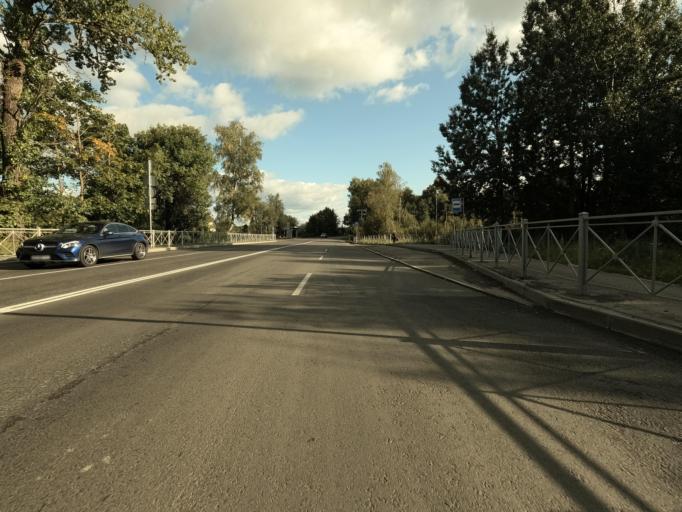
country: RU
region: Leningrad
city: Koltushi
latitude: 59.9370
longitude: 30.6628
